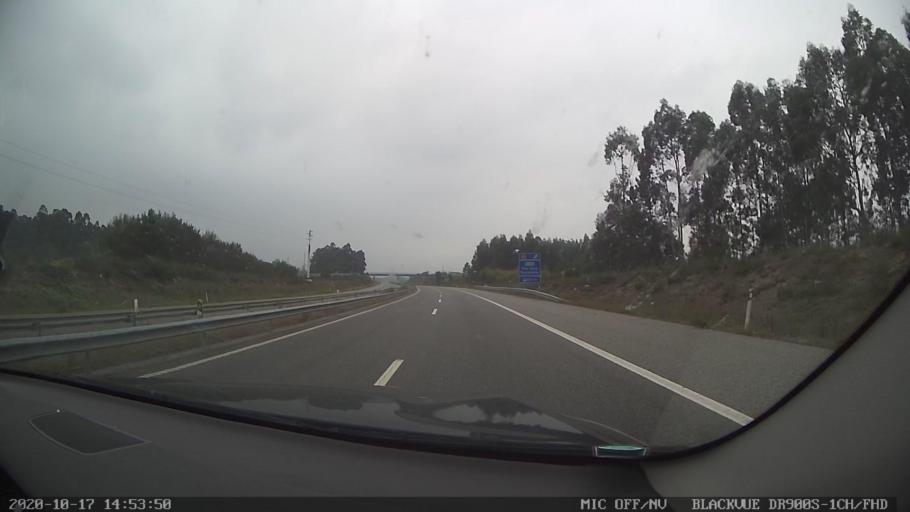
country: PT
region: Braga
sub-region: Barcelos
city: Vila Frescainha
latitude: 41.4995
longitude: -8.6749
